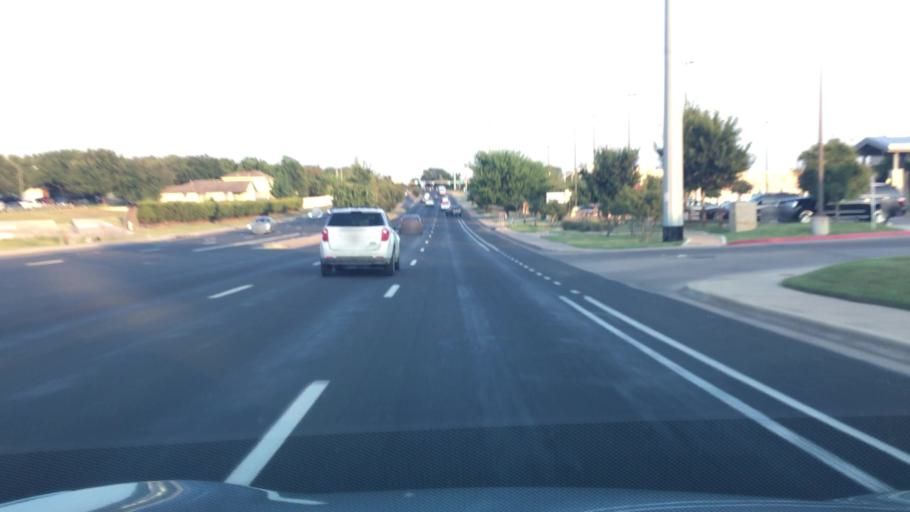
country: US
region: Texas
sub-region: Travis County
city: Onion Creek
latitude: 30.1708
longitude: -97.7977
